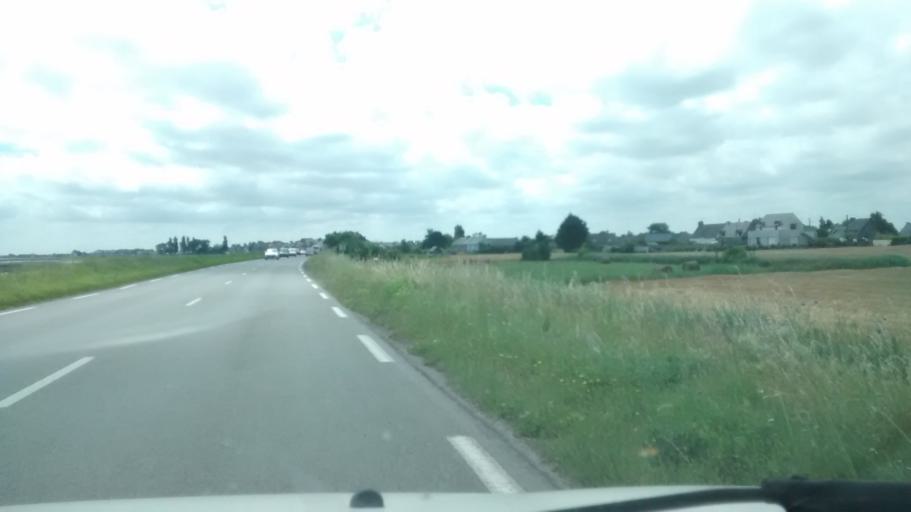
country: FR
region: Brittany
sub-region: Departement d'Ille-et-Vilaine
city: La Fresnais
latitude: 48.6273
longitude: -1.8604
